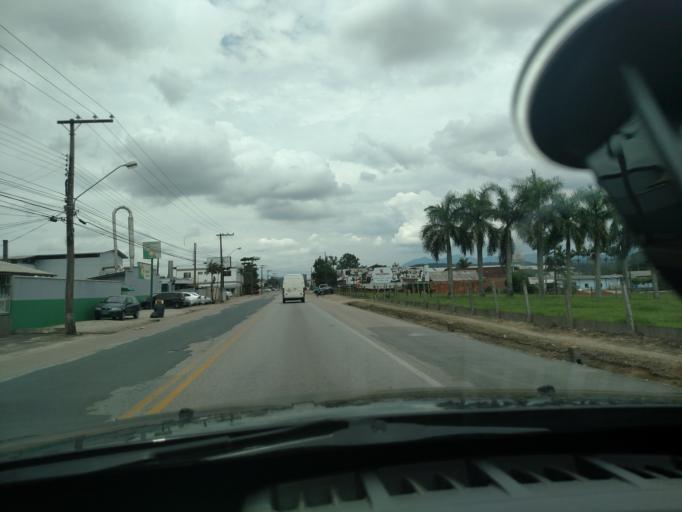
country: BR
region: Santa Catarina
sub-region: Gaspar
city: Gaspar
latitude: -26.9105
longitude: -48.9841
